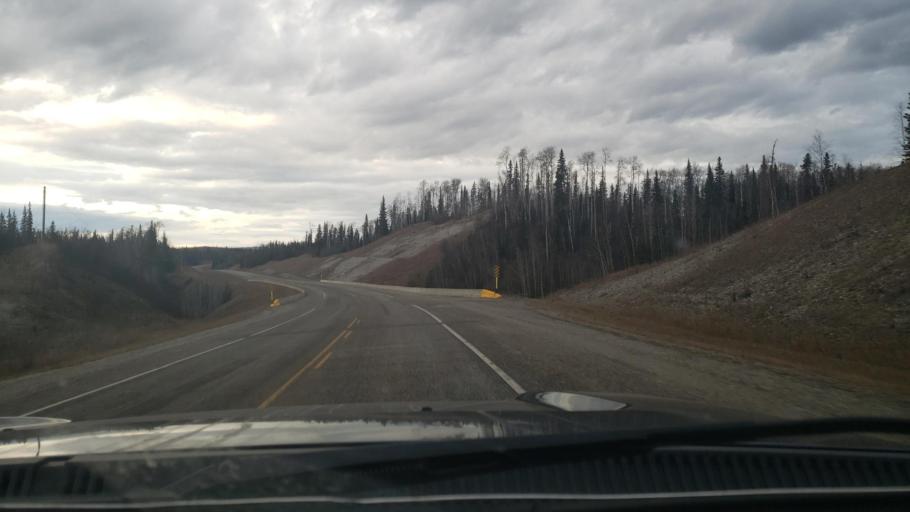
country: CA
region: Yukon
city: Watson Lake
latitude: 59.9784
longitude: -127.5704
